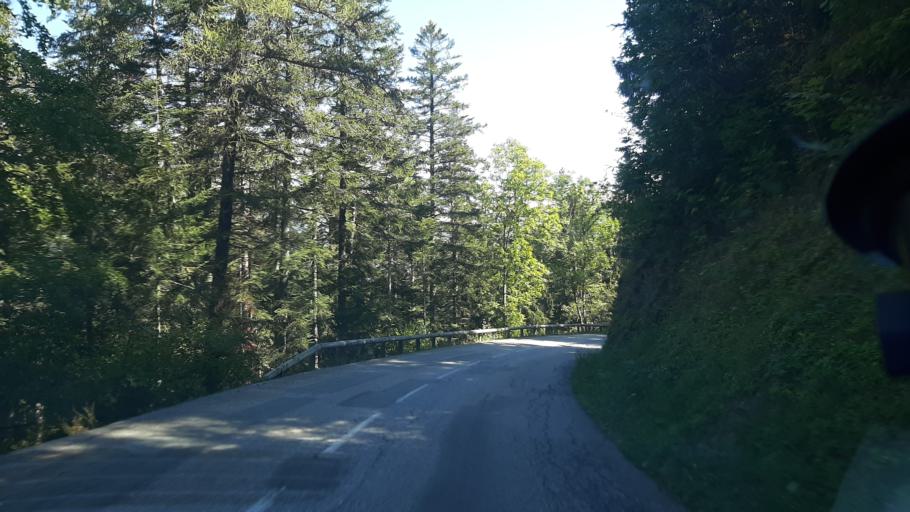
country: FR
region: Rhone-Alpes
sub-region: Departement de la Savoie
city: Aime
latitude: 45.5446
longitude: 6.6482
